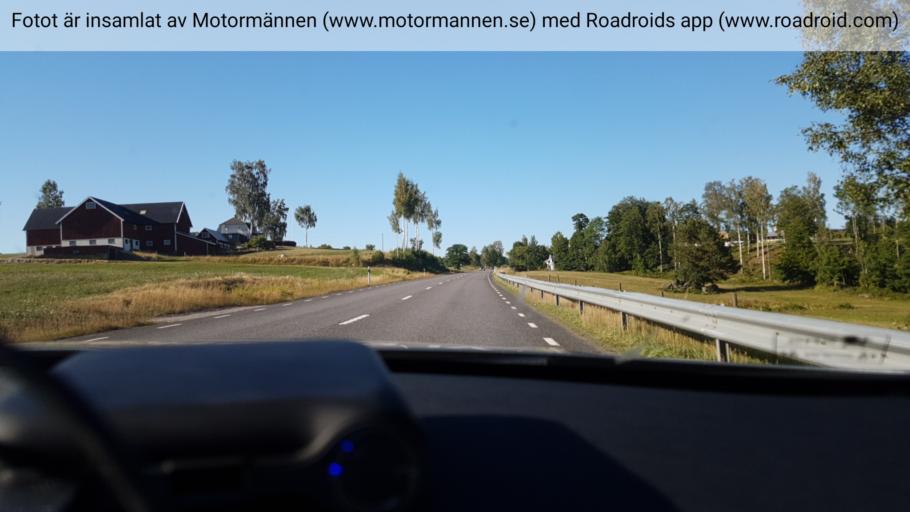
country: SE
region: Joenkoeping
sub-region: Habo Kommun
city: Habo
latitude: 57.9817
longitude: 14.1060
